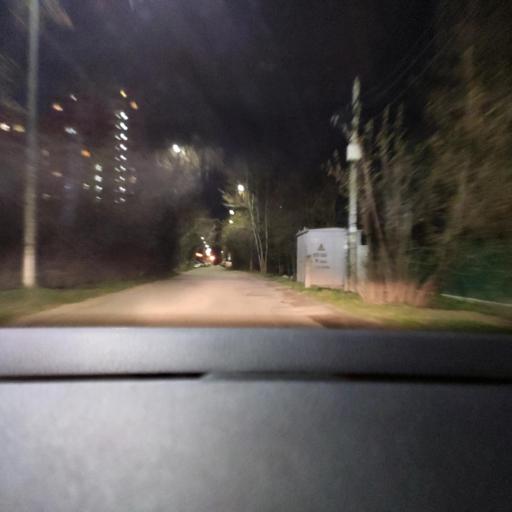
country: RU
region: Moskovskaya
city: Reutov
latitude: 55.7723
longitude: 37.8901
